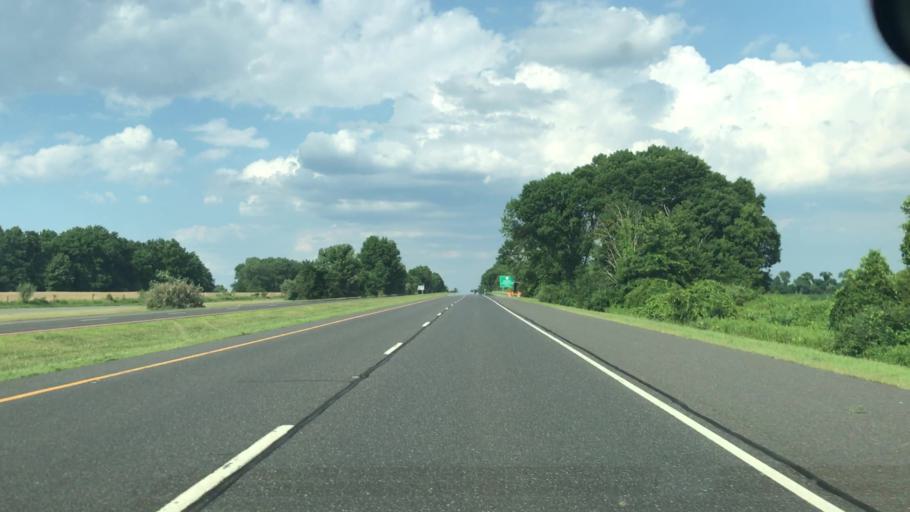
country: US
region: New Jersey
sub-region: Hunterdon County
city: Lambertville
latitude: 40.4099
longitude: -74.8996
